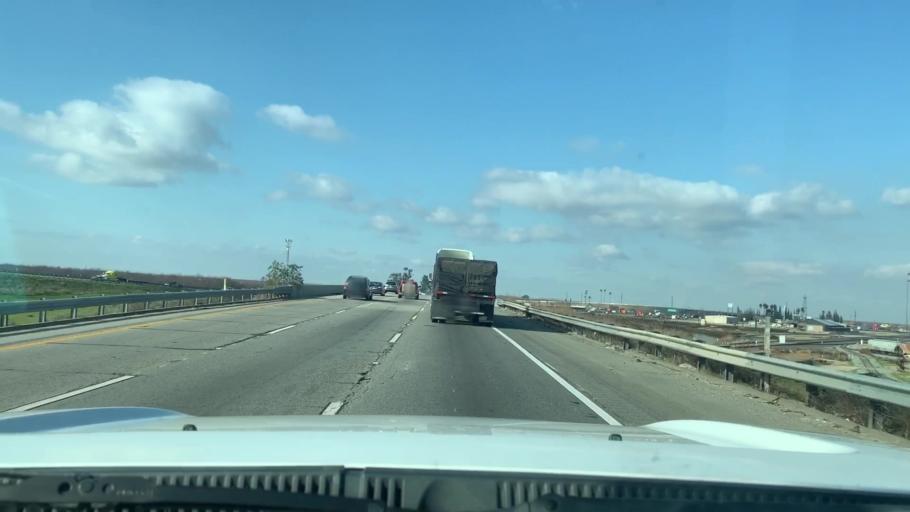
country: US
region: California
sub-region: Kern County
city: McFarland
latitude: 35.5927
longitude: -119.2061
